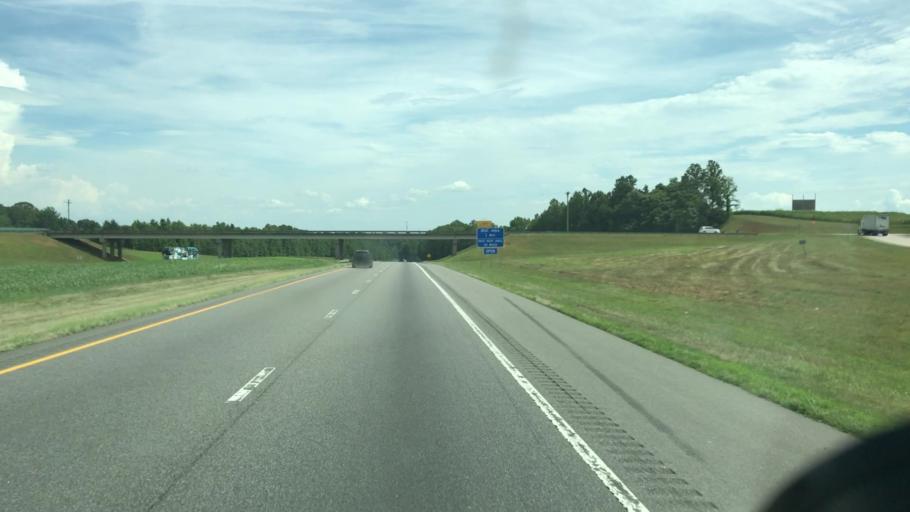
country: US
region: North Carolina
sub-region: Iredell County
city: Statesville
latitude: 35.9192
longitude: -80.8553
